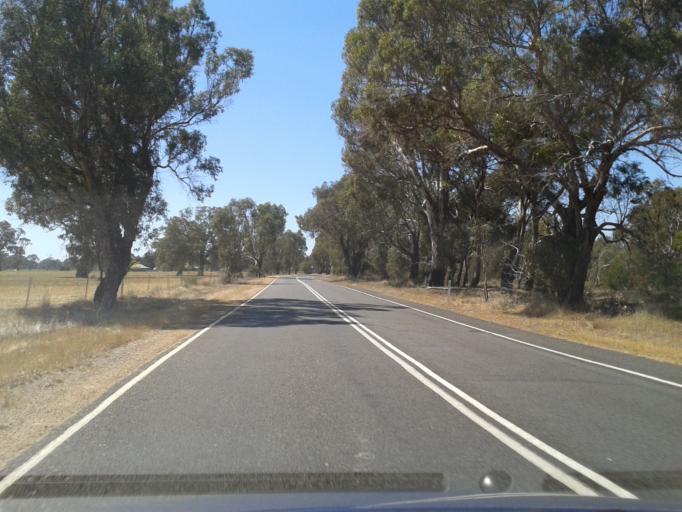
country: AU
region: Victoria
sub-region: Northern Grampians
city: Stawell
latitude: -37.2351
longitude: 142.6867
